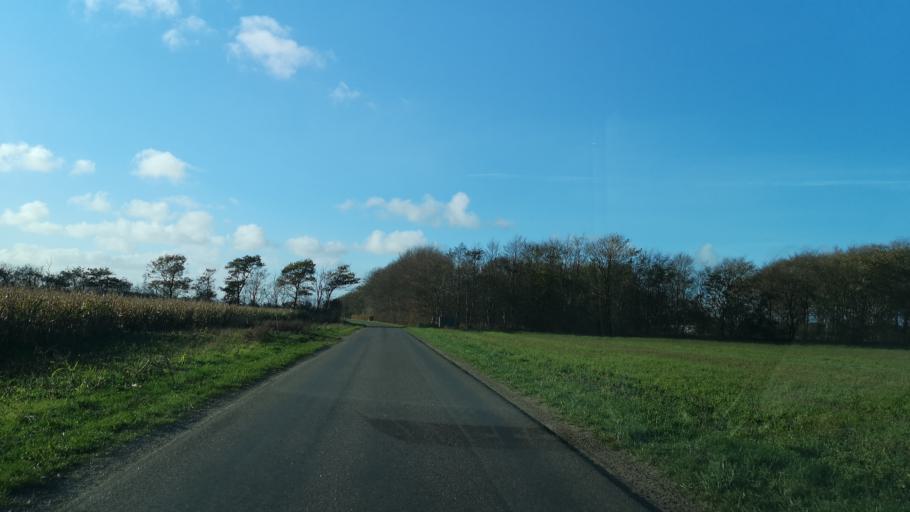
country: DK
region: Central Jutland
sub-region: Ringkobing-Skjern Kommune
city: Tarm
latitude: 55.8289
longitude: 8.3880
